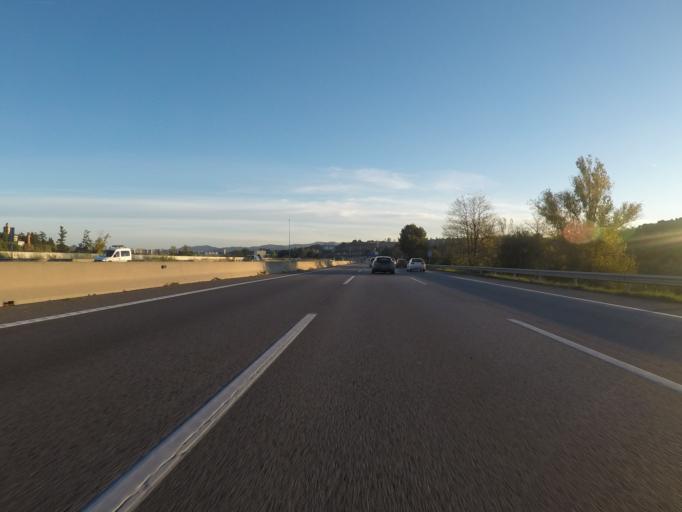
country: ES
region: Catalonia
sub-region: Provincia de Barcelona
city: Sant Quirze del Valles
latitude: 41.5224
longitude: 2.0969
